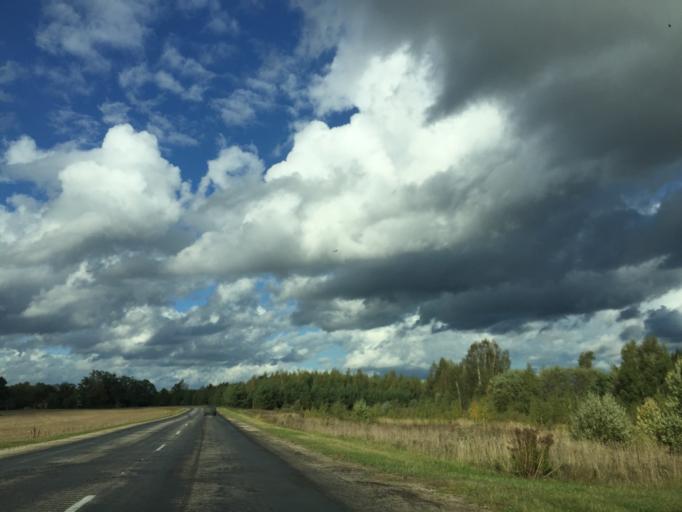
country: LV
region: Malpils
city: Malpils
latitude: 57.0007
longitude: 24.9104
